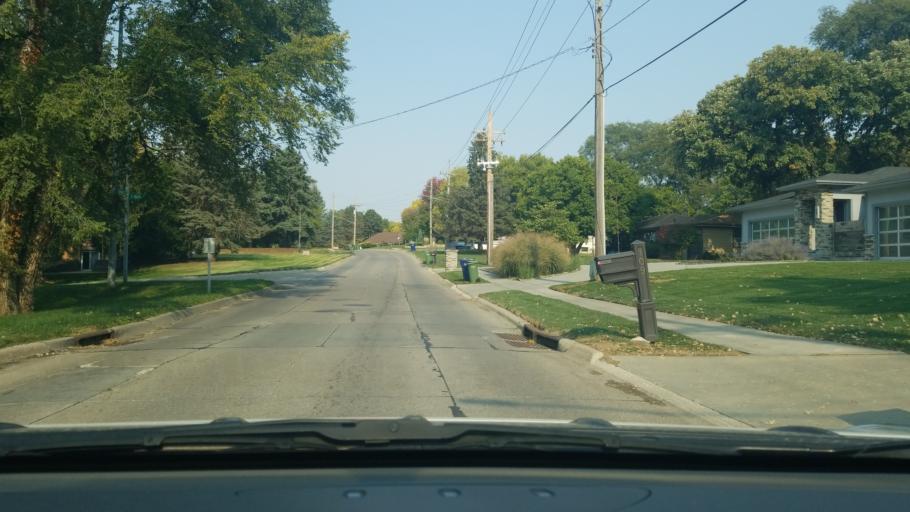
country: US
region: Nebraska
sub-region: Sarpy County
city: Bellevue
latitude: 41.1617
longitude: -95.9101
